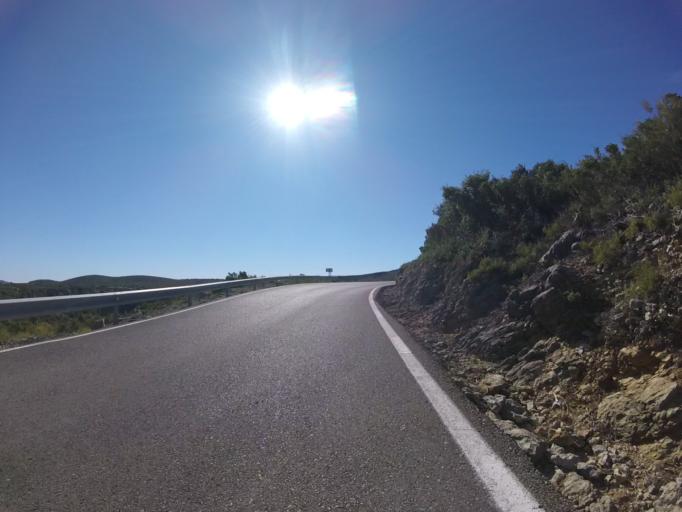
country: ES
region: Valencia
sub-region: Provincia de Castello
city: Albocasser
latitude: 40.3929
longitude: 0.0403
